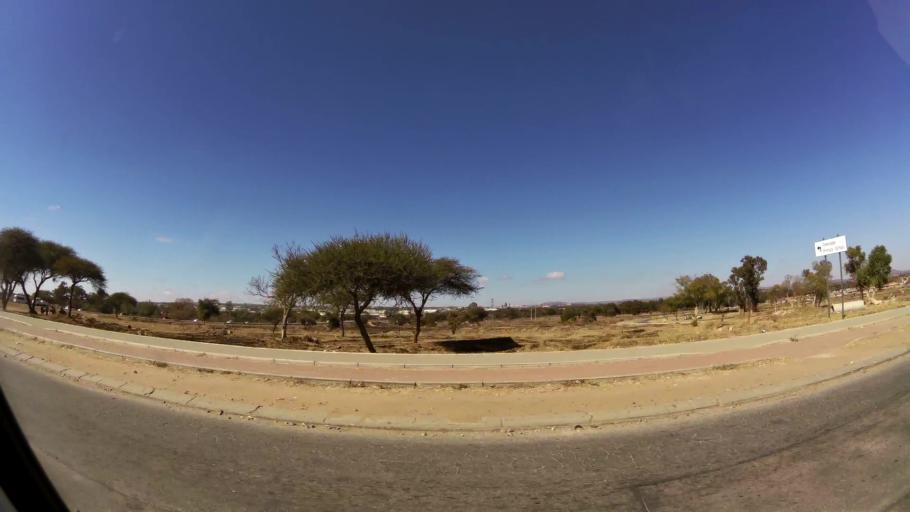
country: ZA
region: Limpopo
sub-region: Capricorn District Municipality
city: Polokwane
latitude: -23.8847
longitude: 29.4239
